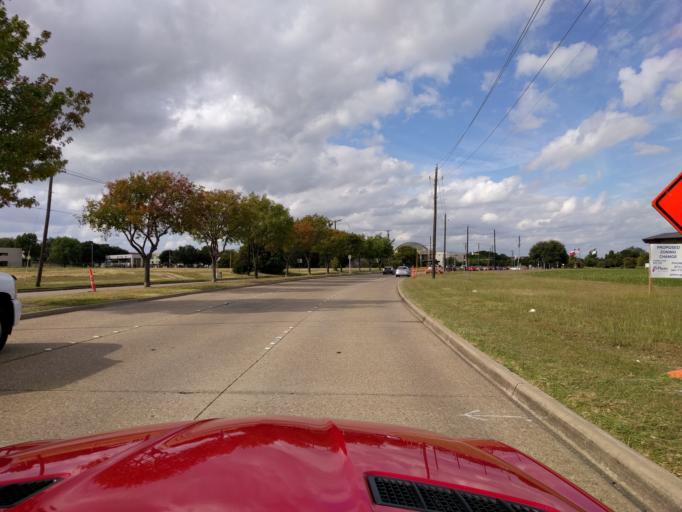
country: US
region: Texas
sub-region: Collin County
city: Plano
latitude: 33.0054
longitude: -96.7333
